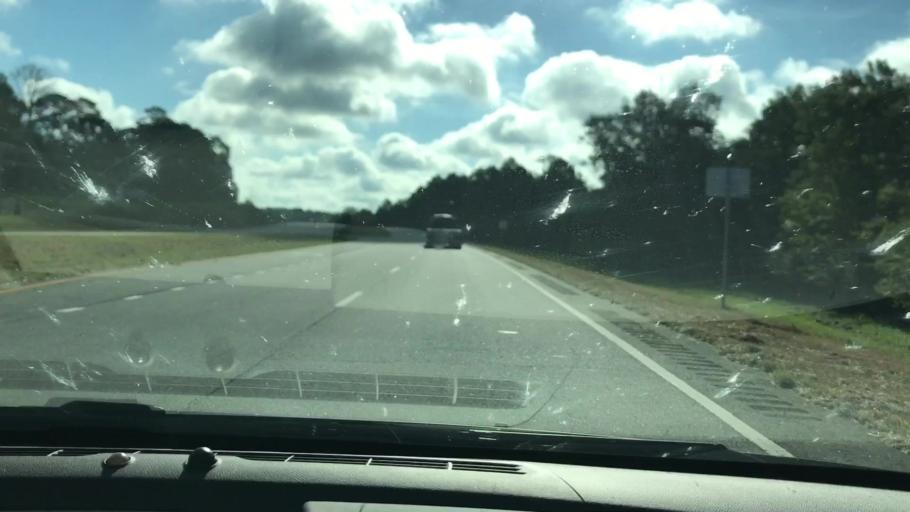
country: US
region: Georgia
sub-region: Worth County
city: Sylvester
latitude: 31.5504
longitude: -83.9683
